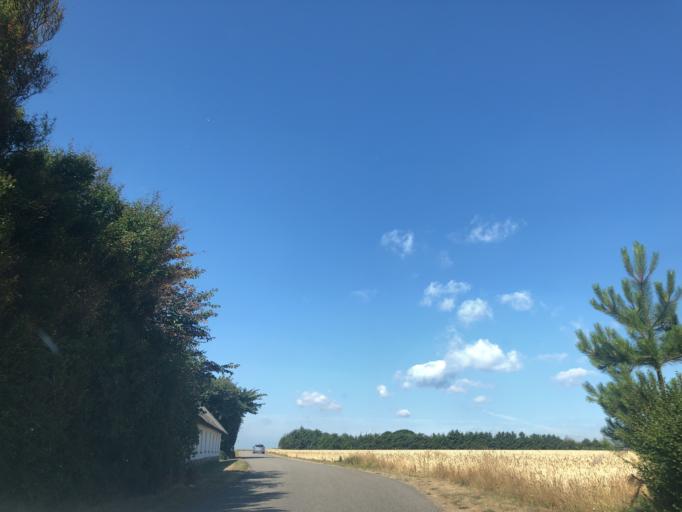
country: DK
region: North Denmark
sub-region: Morso Kommune
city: Nykobing Mors
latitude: 56.8056
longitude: 8.9966
